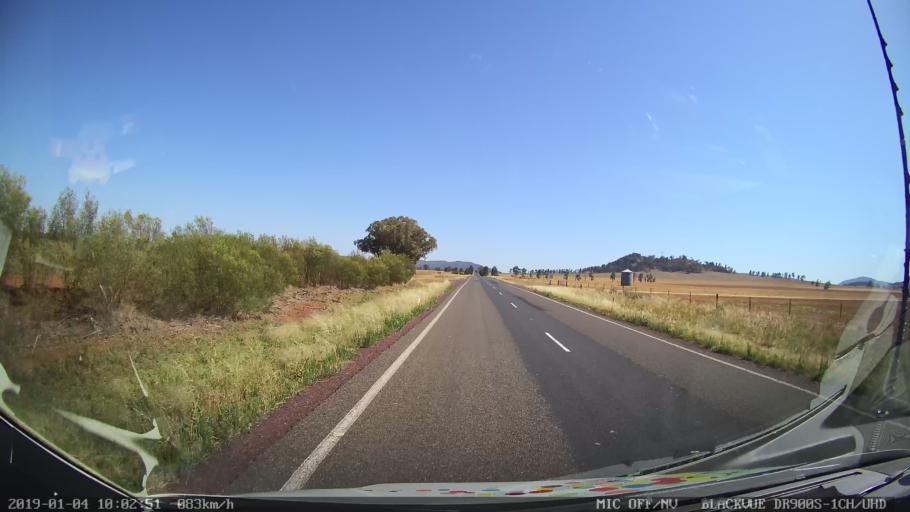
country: AU
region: New South Wales
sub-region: Cabonne
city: Canowindra
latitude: -33.4711
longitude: 148.3650
